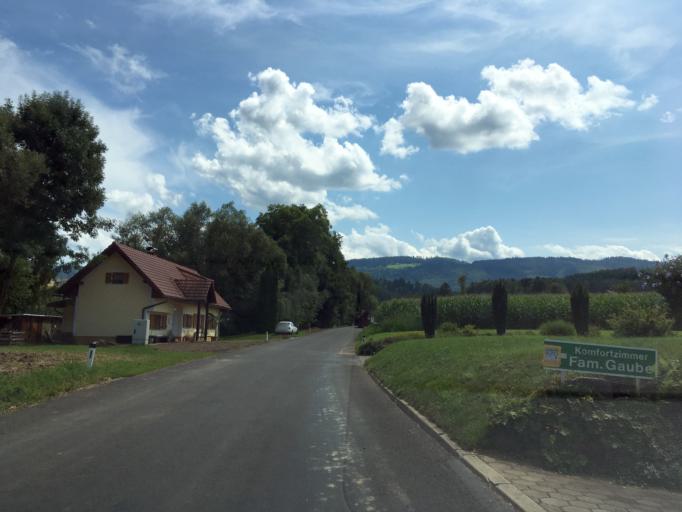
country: AT
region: Styria
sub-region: Politischer Bezirk Leibnitz
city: Oberhaag
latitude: 46.6840
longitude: 15.3524
